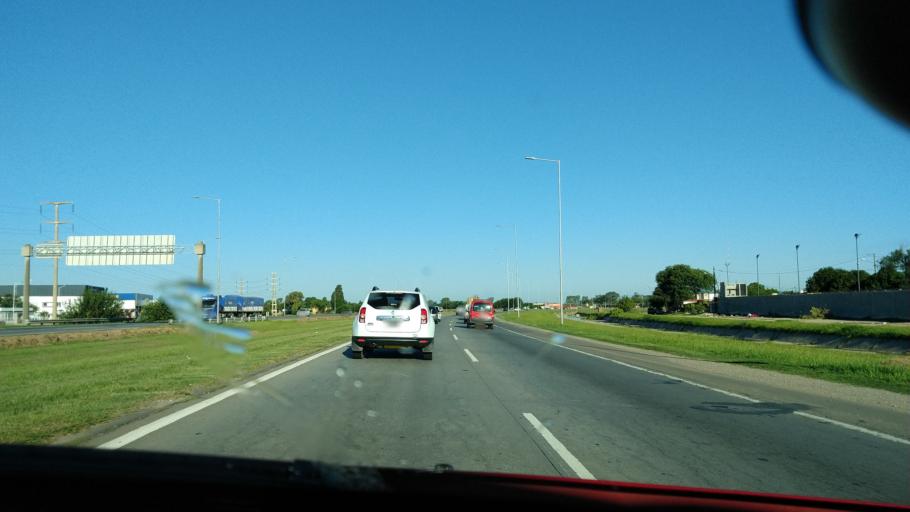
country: AR
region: Cordoba
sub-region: Departamento de Capital
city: Cordoba
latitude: -31.3638
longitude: -64.1372
